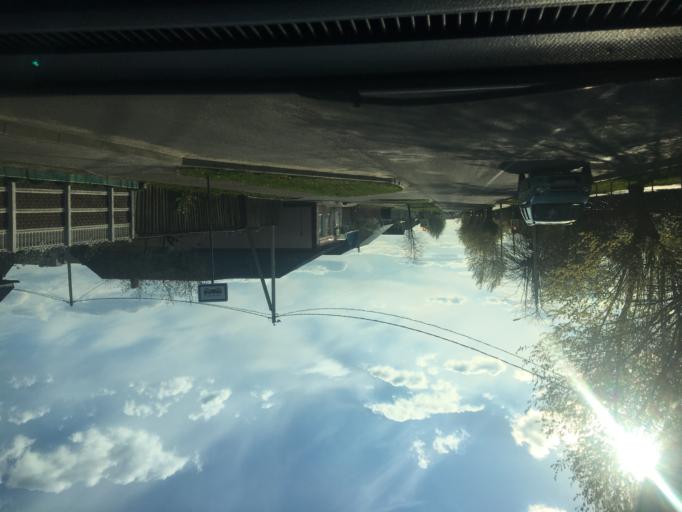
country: BY
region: Mogilev
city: Babruysk
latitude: 53.1471
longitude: 29.1997
